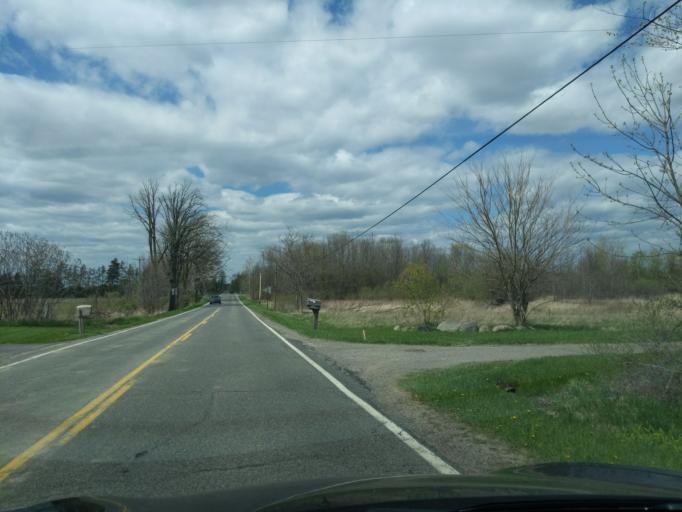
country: US
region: Michigan
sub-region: Ingham County
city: Mason
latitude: 42.6163
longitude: -84.4574
